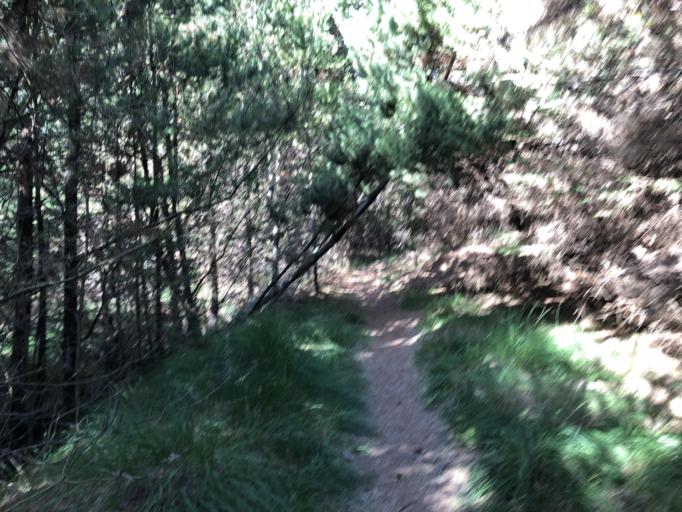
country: DK
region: Central Jutland
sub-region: Holstebro Kommune
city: Ulfborg
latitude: 56.2899
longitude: 8.1397
